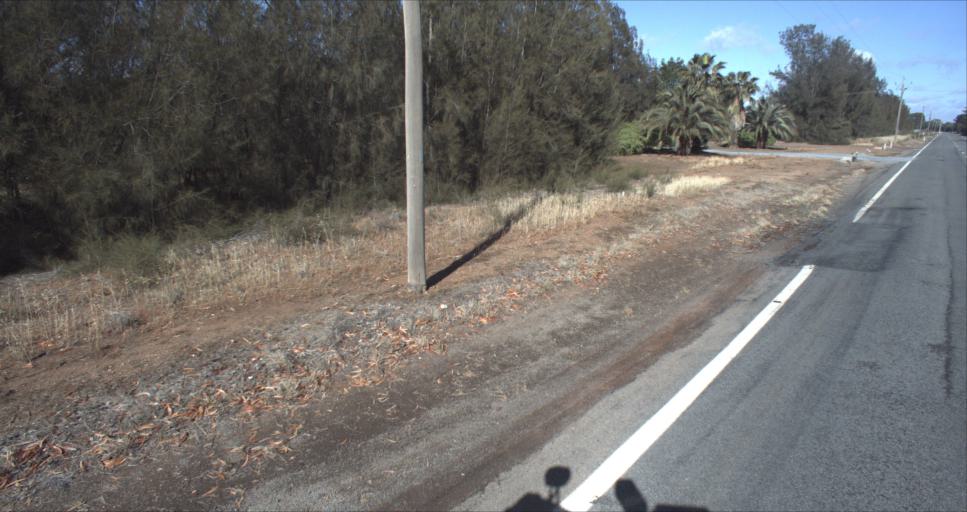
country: AU
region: New South Wales
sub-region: Leeton
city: Leeton
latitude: -34.5448
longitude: 146.3513
